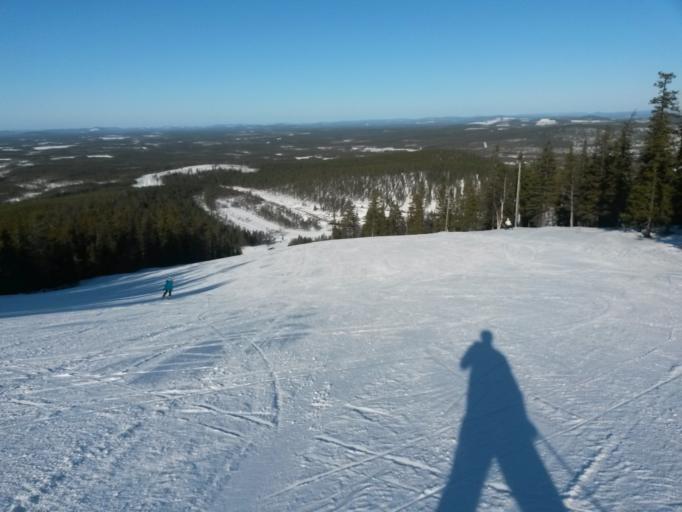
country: SE
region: Vaesterbotten
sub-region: Skelleftea Kommun
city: Langsele
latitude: 65.1560
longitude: 20.1370
